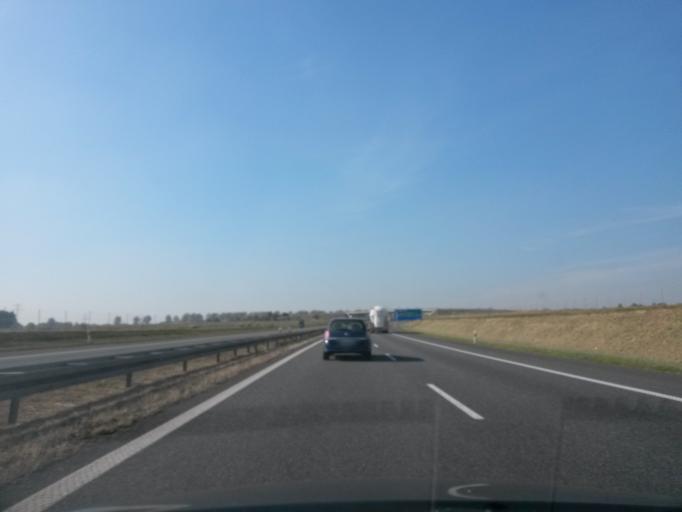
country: PL
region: Silesian Voivodeship
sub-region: Powiat gliwicki
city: Zernica
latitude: 50.2663
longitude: 18.5921
